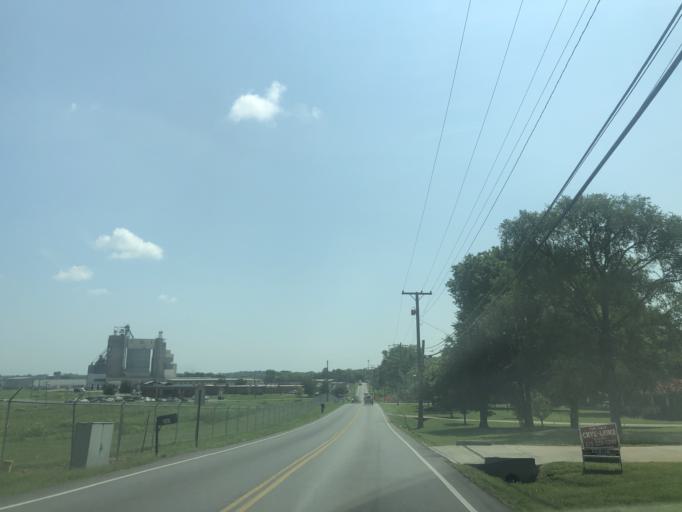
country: US
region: Tennessee
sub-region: Rutherford County
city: La Vergne
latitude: 36.0153
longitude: -86.5889
